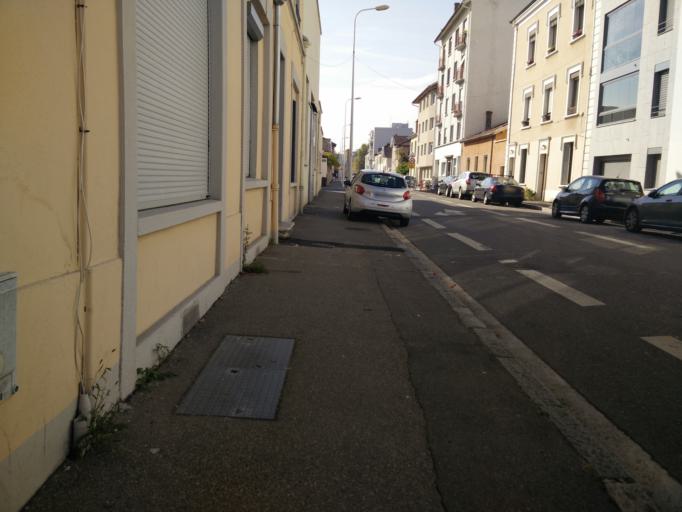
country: FR
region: Rhone-Alpes
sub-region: Departement du Rhone
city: Villeurbanne
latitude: 45.7530
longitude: 4.8853
